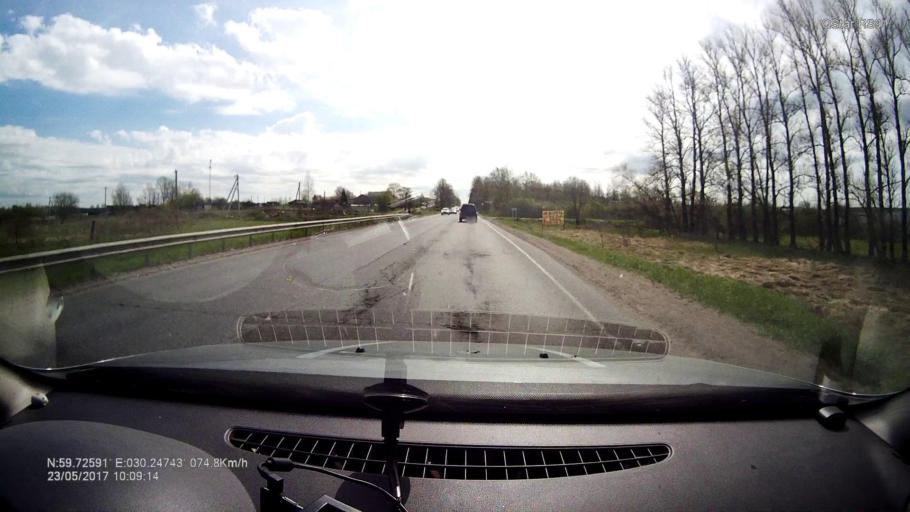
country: RU
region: St.-Petersburg
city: Aleksandrovskaya
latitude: 59.7251
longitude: 30.2475
